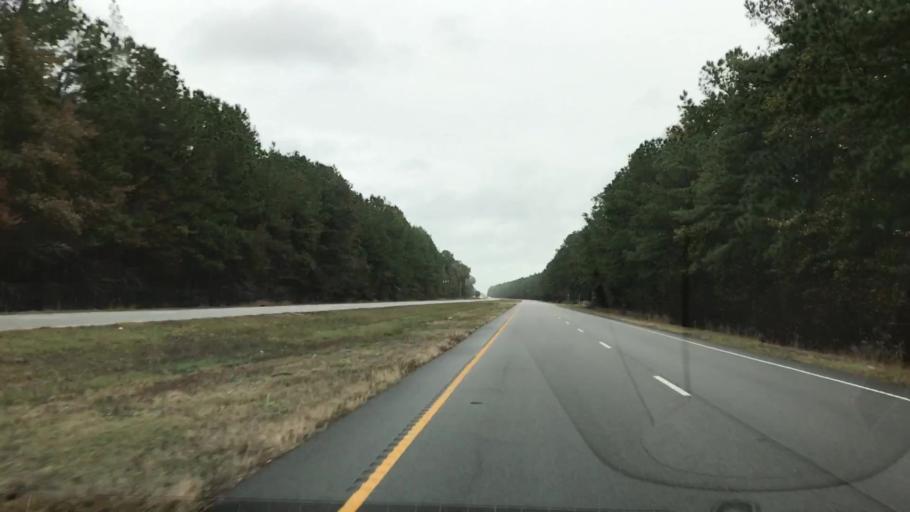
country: US
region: South Carolina
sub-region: Charleston County
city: Awendaw
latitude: 33.1189
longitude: -79.4542
